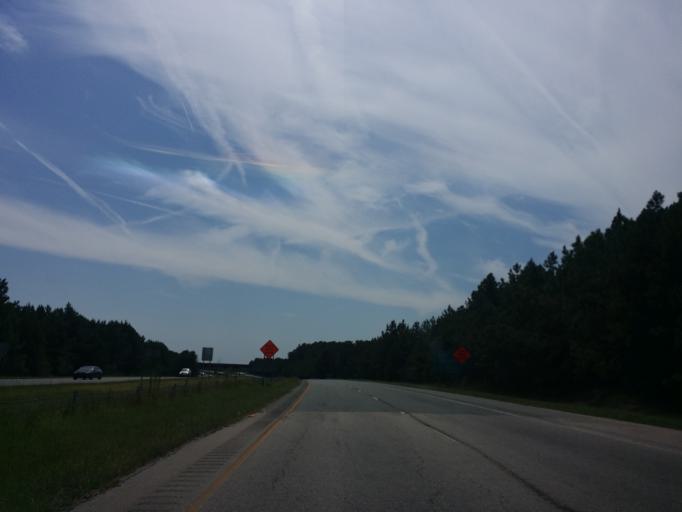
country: US
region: North Carolina
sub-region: Wake County
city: Morrisville
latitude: 35.8997
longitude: -78.8126
